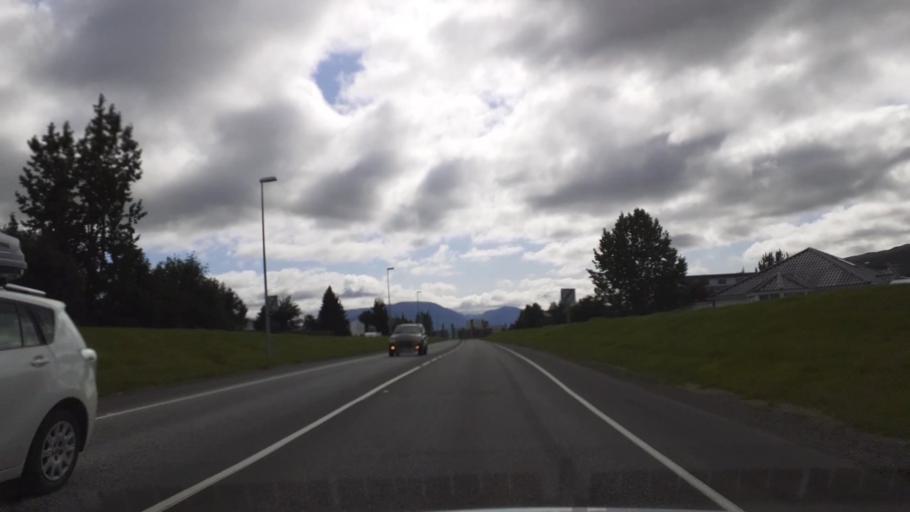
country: IS
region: Northeast
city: Akureyri
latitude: 65.6737
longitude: -18.1092
